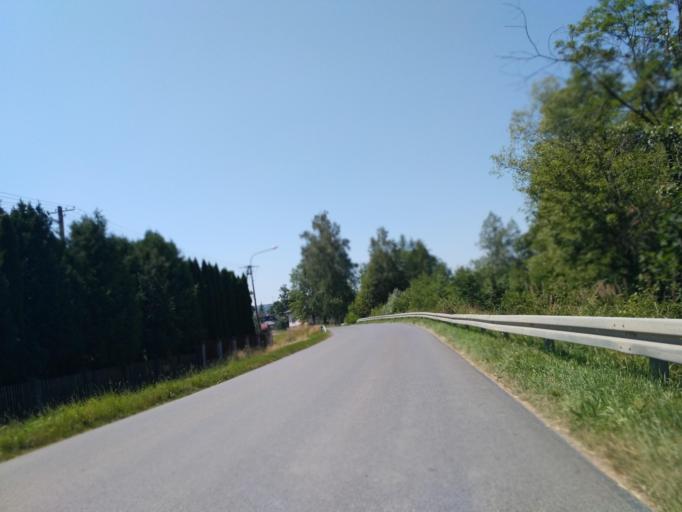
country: PL
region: Subcarpathian Voivodeship
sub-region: Powiat sanocki
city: Niebieszczany
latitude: 49.5339
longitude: 22.1280
